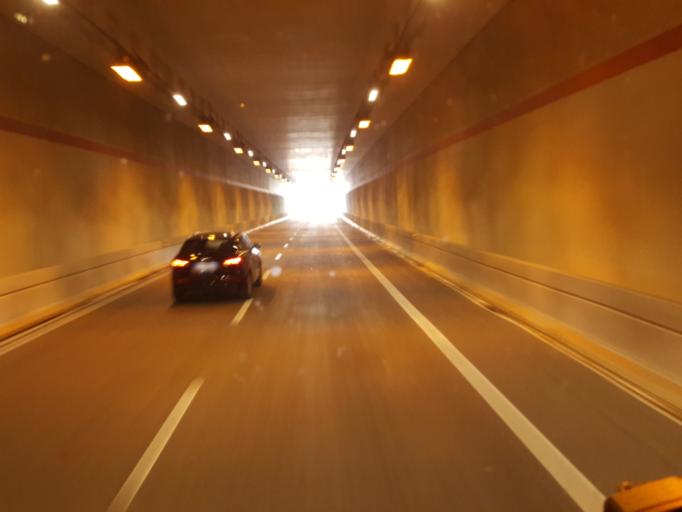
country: IT
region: Apulia
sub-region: Provincia di Bari
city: Palo del Colle
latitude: 41.0482
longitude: 16.7121
